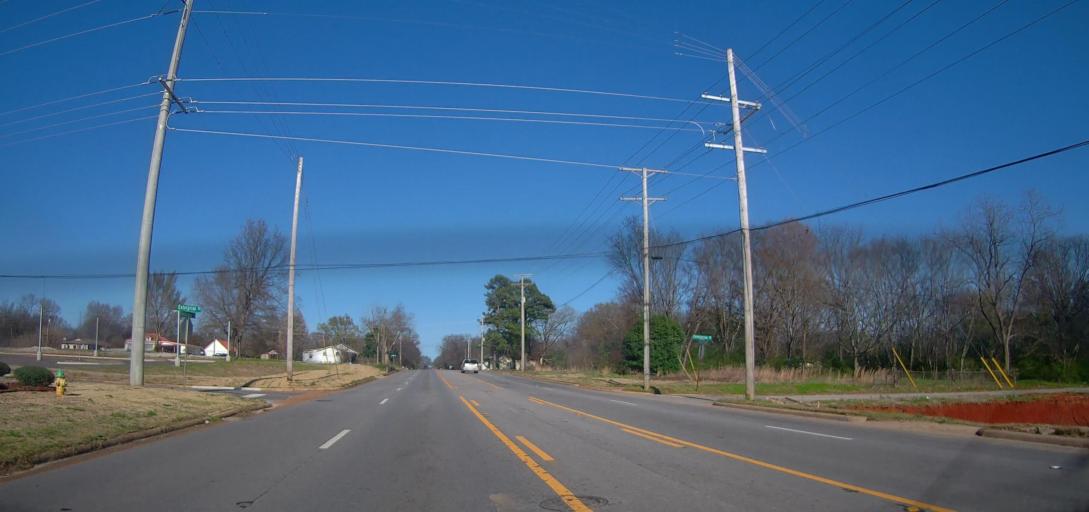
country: US
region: Alabama
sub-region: Lauderdale County
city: East Florence
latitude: 34.8046
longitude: -87.6482
